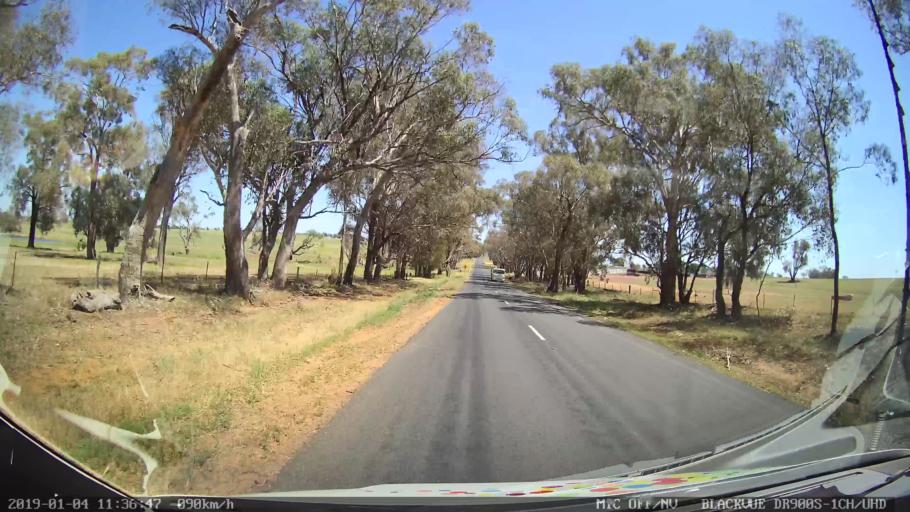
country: AU
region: New South Wales
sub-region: Cabonne
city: Molong
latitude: -33.0399
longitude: 148.8126
